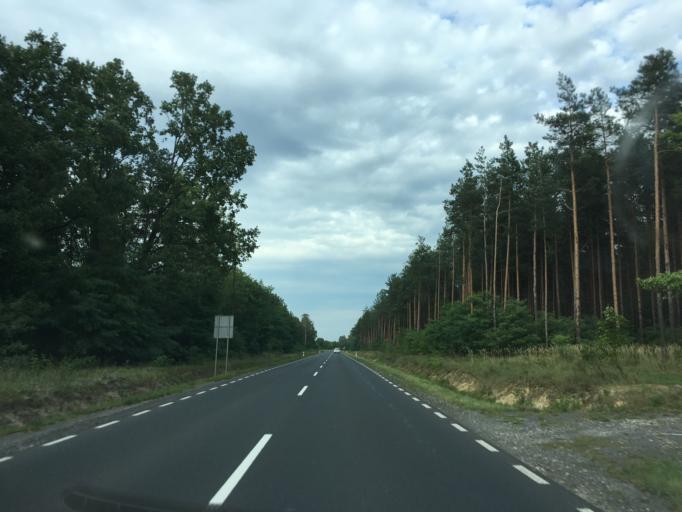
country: PL
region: Swietokrzyskie
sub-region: Powiat wloszczowski
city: Secemin
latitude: 50.7770
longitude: 19.8802
